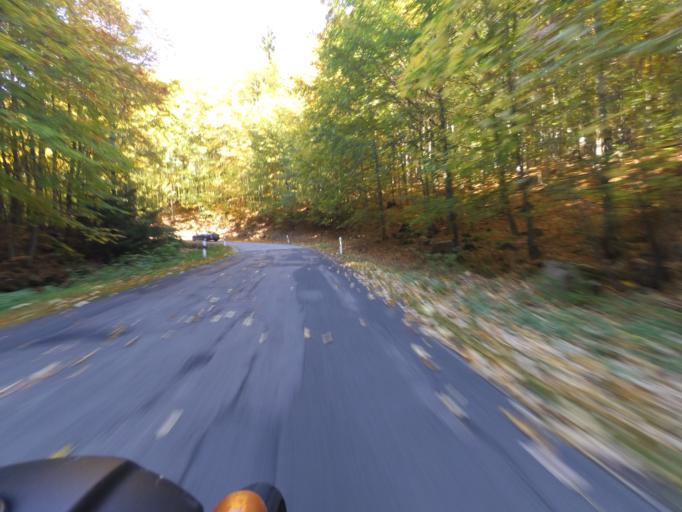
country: DE
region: Saxony
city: Altenberg
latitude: 50.7956
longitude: 13.7547
